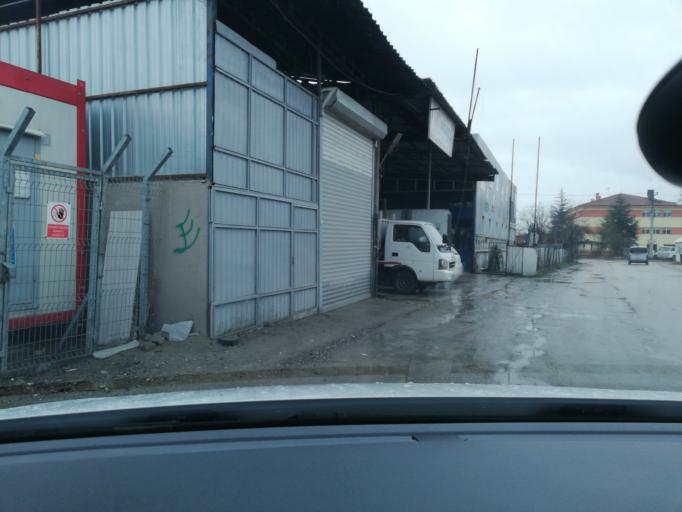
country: TR
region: Bolu
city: Bolu
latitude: 40.7376
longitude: 31.6307
